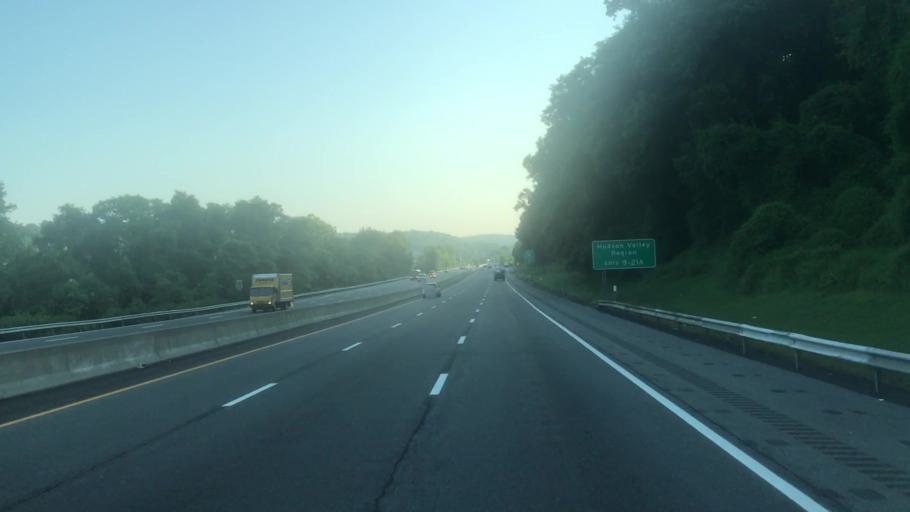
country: US
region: New York
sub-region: Westchester County
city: Ardsley
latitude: 41.0015
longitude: -73.8529
